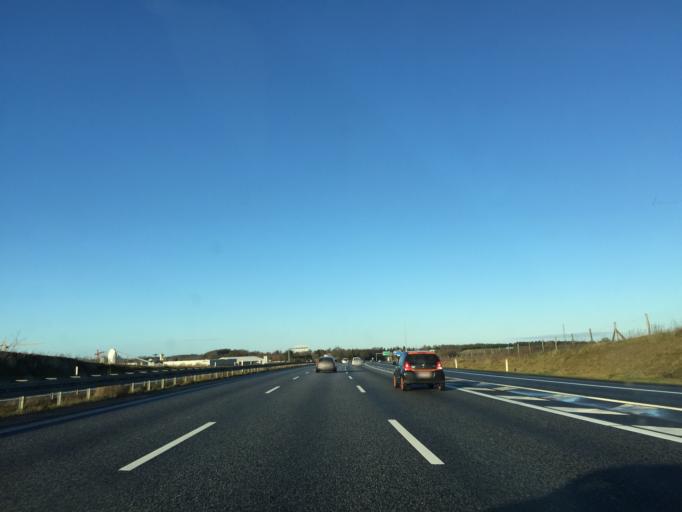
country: DK
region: South Denmark
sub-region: Vejle Kommune
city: Vejle
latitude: 55.6647
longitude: 9.5549
